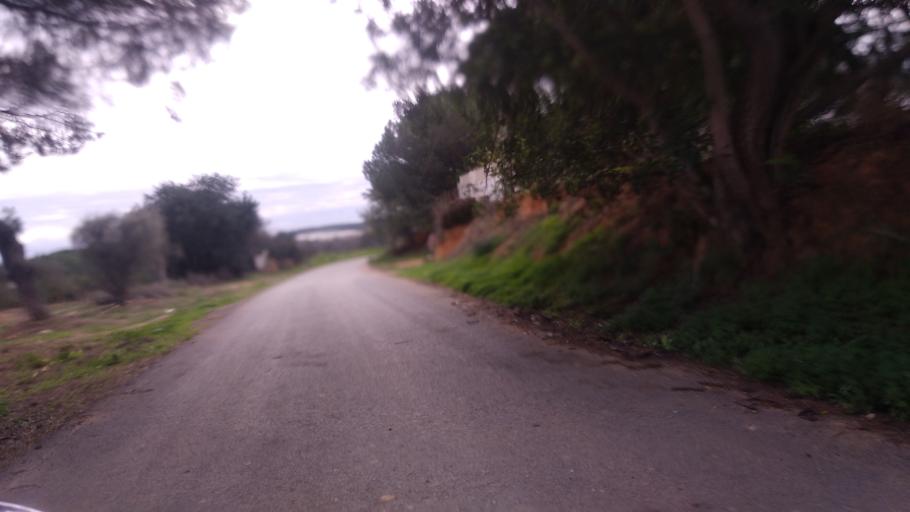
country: PT
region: Faro
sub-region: Faro
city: Santa Barbara de Nexe
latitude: 37.0703
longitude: -7.9716
